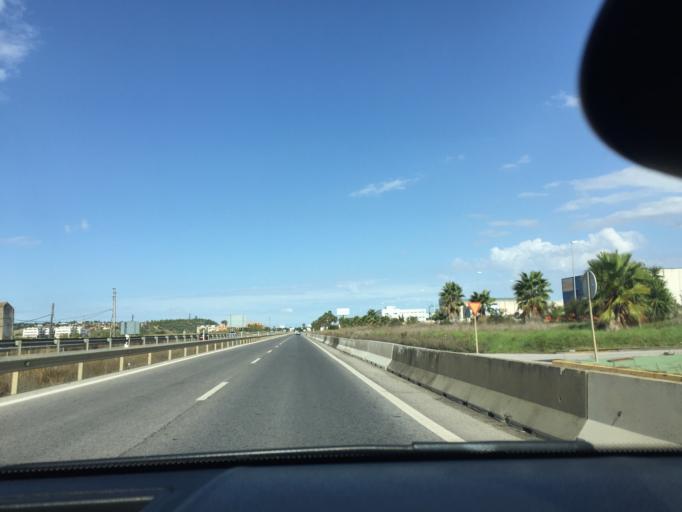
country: ES
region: Andalusia
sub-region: Provincia de Sevilla
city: Gelves
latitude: 37.3153
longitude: -6.0350
